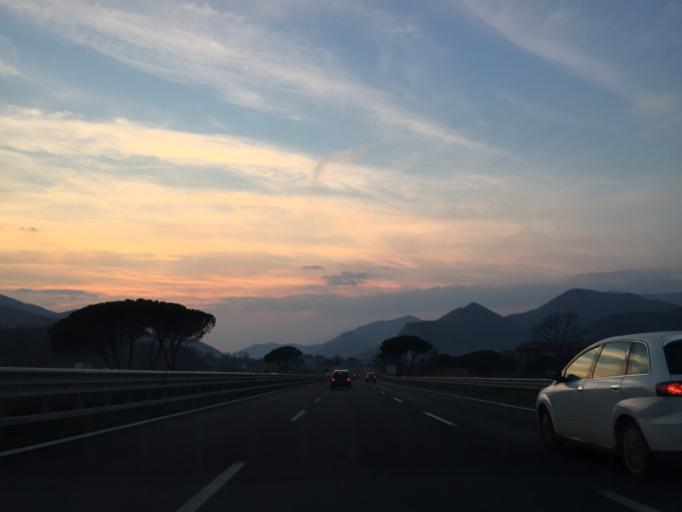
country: IT
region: Campania
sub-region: Provincia di Salerno
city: Faraldo-Nocelleto
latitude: 40.7733
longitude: 14.7690
